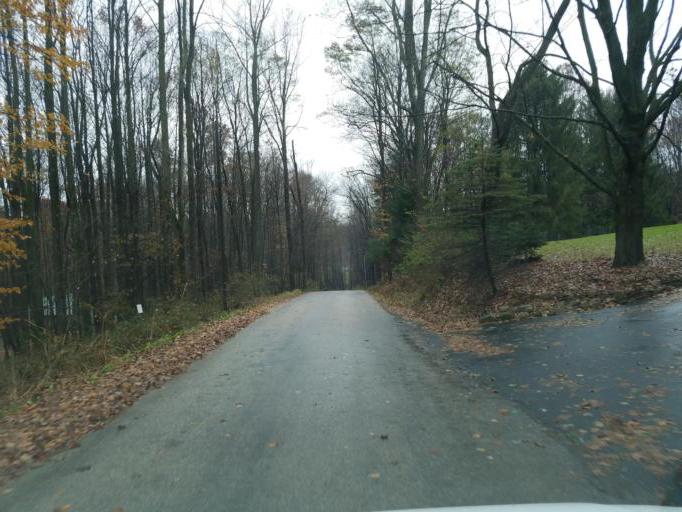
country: US
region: Ohio
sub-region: Richland County
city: Ontario
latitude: 40.7235
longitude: -82.6022
